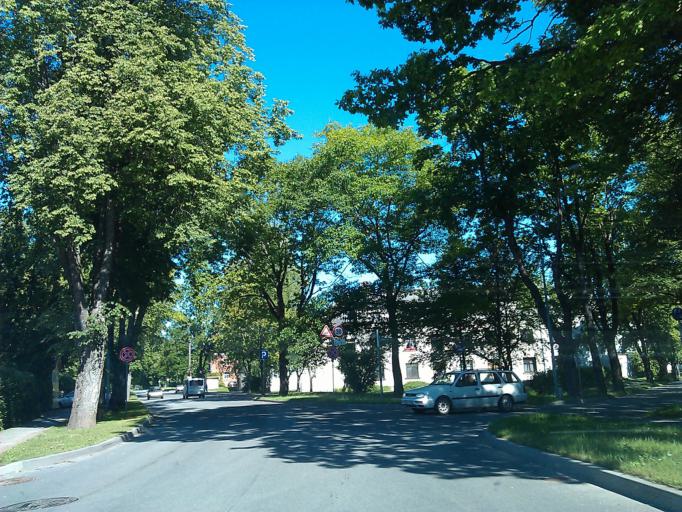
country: LV
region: Cesu Rajons
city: Cesis
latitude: 57.3088
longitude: 25.2505
